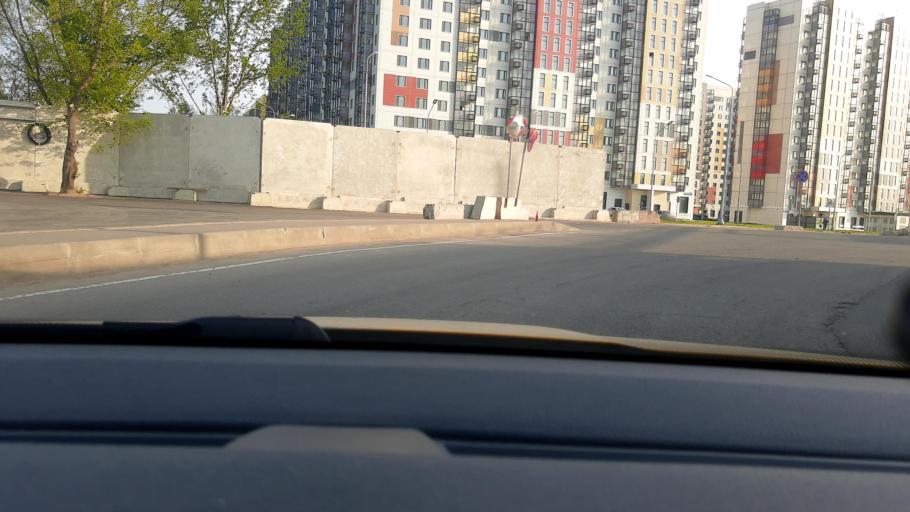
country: RU
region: Moscow
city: Severnyy
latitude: 55.9437
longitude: 37.5303
